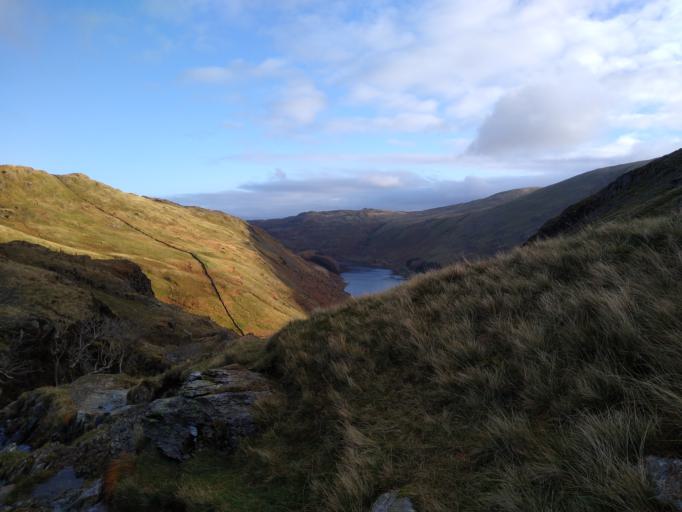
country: GB
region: England
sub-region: Cumbria
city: Windermere
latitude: 54.4838
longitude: -2.8389
